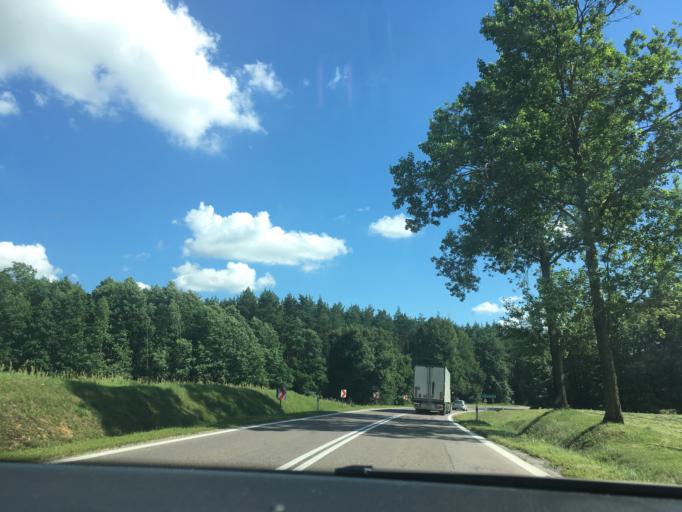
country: PL
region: Podlasie
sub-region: Powiat sokolski
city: Suchowola
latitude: 53.6219
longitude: 23.1252
